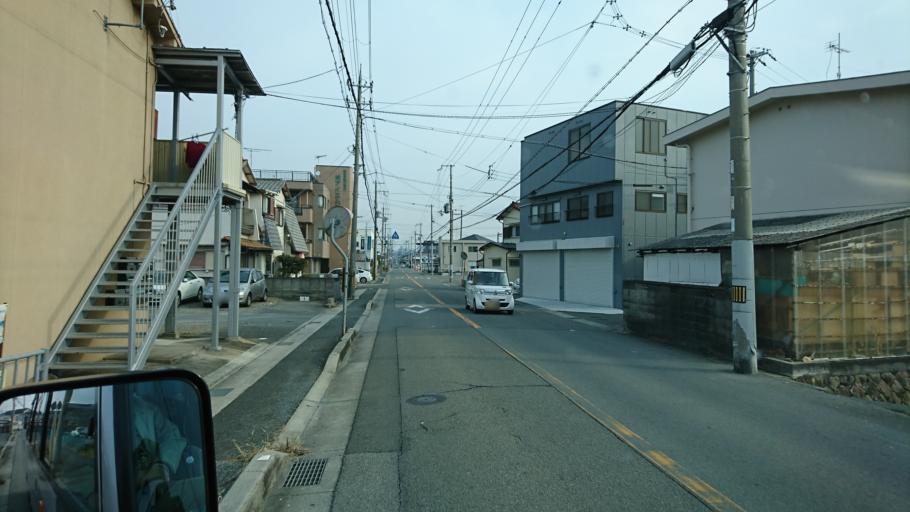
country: JP
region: Hyogo
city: Kakogawacho-honmachi
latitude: 34.7961
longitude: 134.8137
